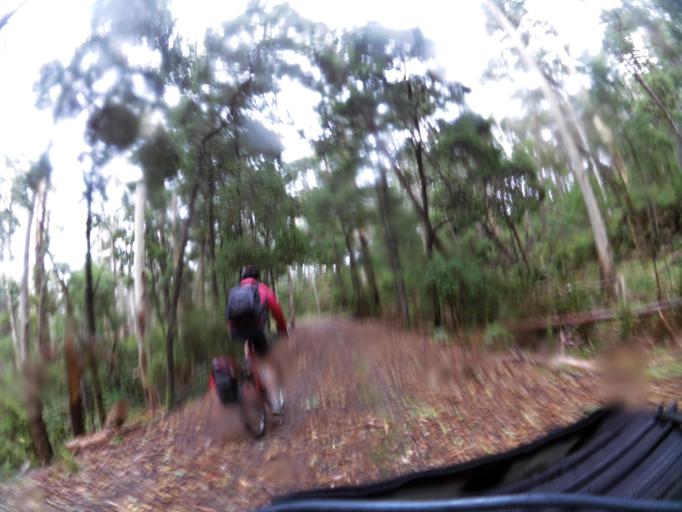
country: AU
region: New South Wales
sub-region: Greater Hume Shire
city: Holbrook
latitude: -36.1904
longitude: 147.5075
